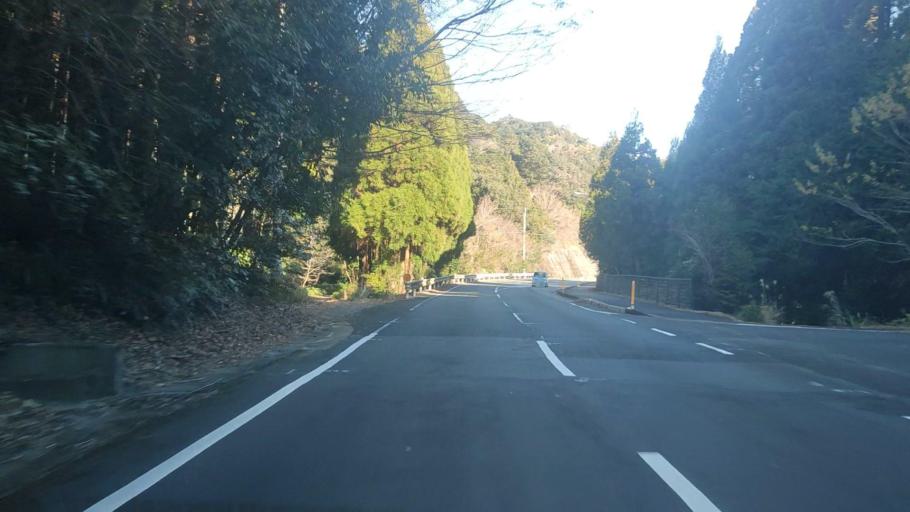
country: JP
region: Miyazaki
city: Nobeoka
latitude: 32.6951
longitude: 131.8120
